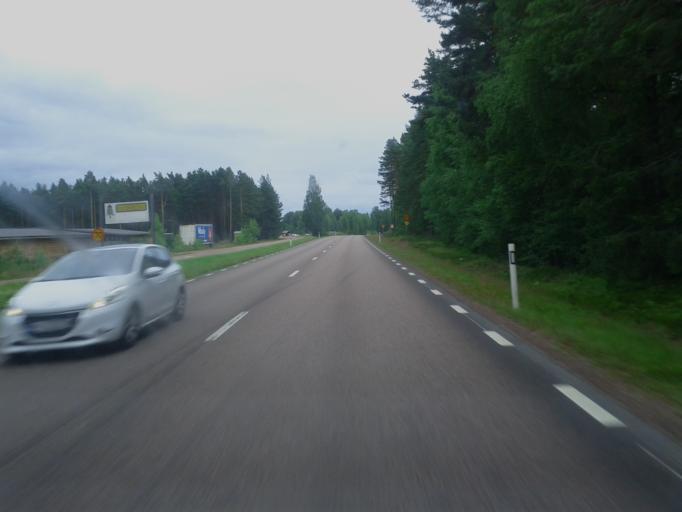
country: SE
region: Dalarna
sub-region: Mora Kommun
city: Mora
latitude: 61.0422
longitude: 14.5032
